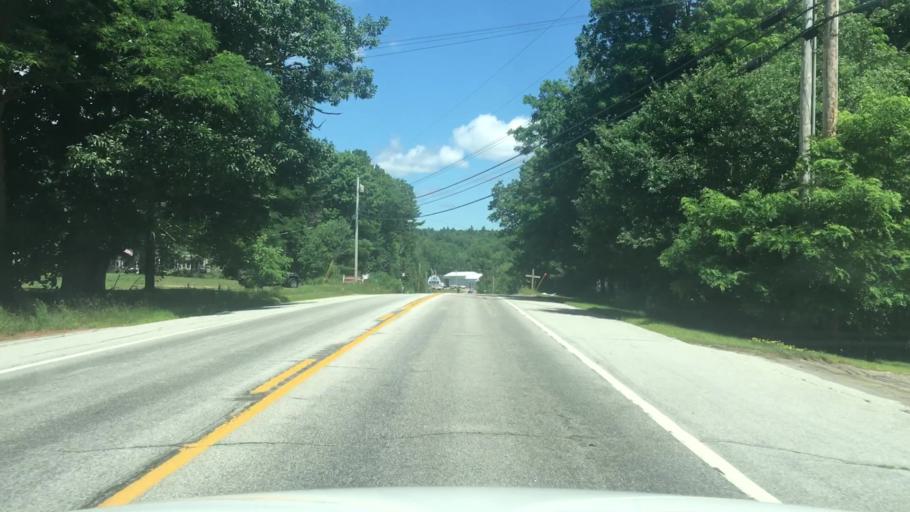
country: US
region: Maine
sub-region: Waldo County
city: Northport
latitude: 44.3502
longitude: -68.9686
